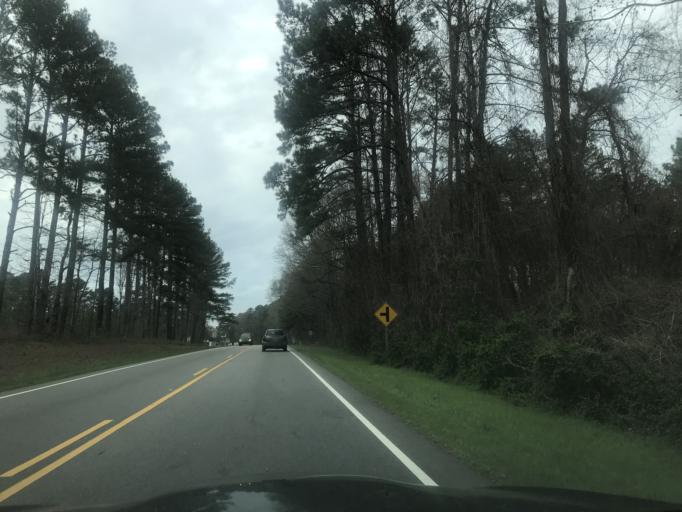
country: US
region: North Carolina
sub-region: Franklin County
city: Franklinton
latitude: 36.1002
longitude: -78.4265
